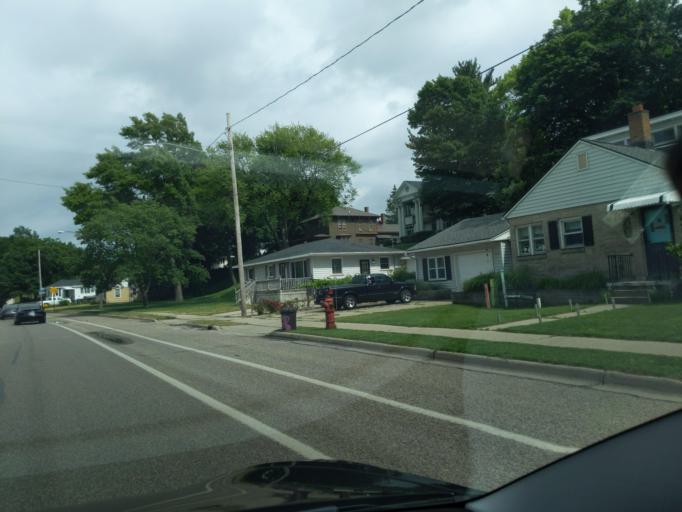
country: US
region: Michigan
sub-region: Muskegon County
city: Roosevelt Park
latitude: 43.2140
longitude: -86.2995
